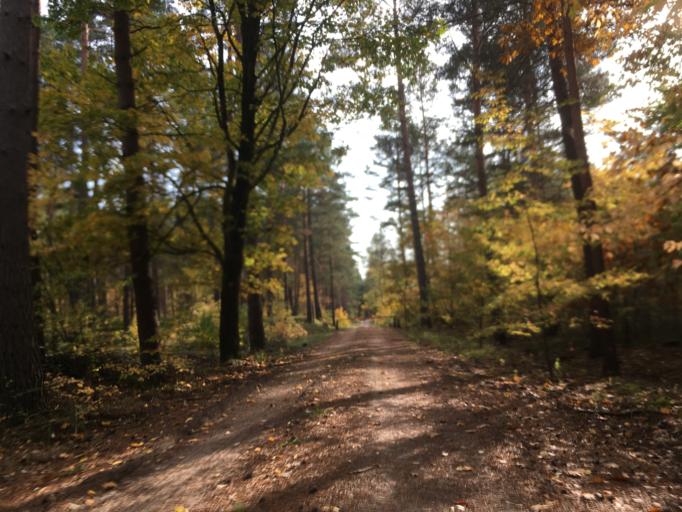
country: DE
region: Brandenburg
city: Liebenwalde
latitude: 52.9322
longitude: 13.5037
